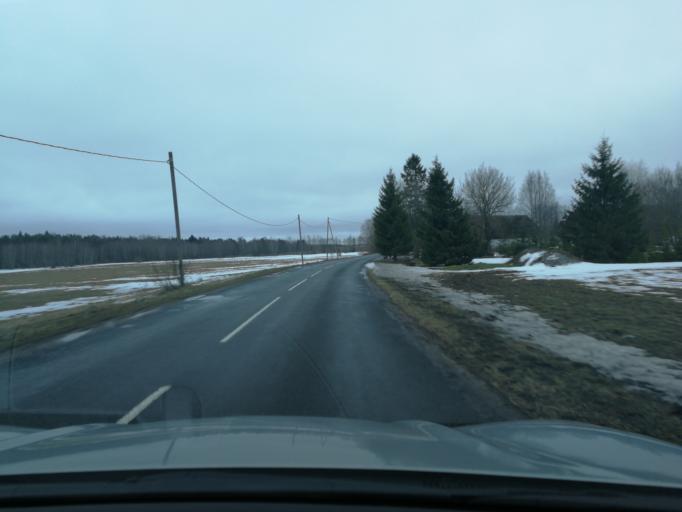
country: EE
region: Harju
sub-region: Kiili vald
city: Kiili
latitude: 59.2873
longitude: 24.8762
